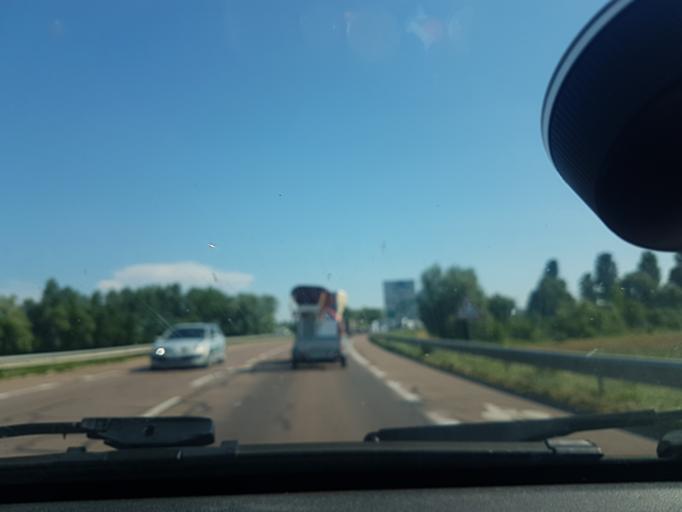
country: FR
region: Bourgogne
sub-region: Departement de Saone-et-Loire
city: Saint-Marcel
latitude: 46.7794
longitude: 4.8767
